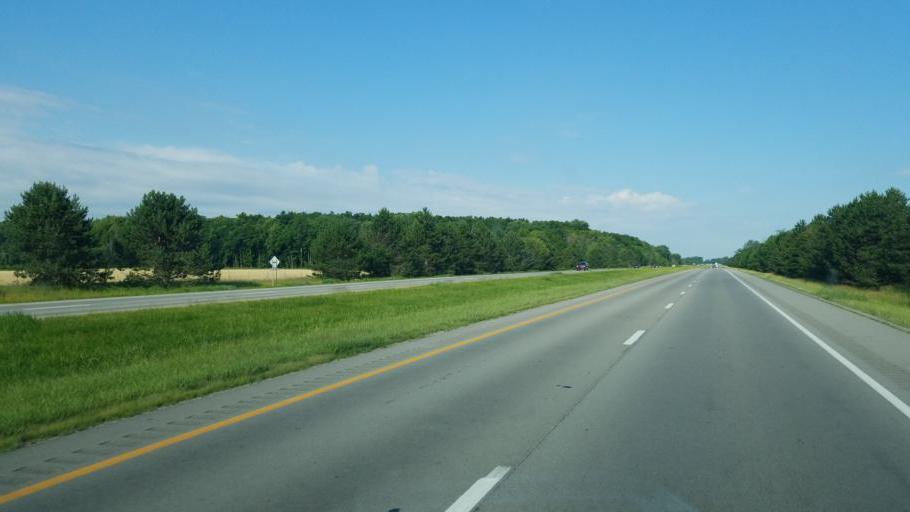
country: US
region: Ohio
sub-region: Wyandot County
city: Carey
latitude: 40.9820
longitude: -83.5140
